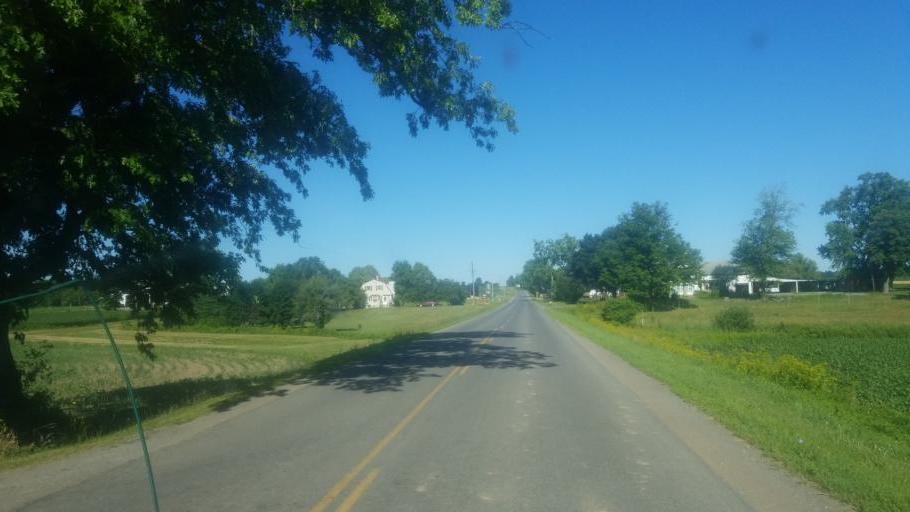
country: US
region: New York
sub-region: Ontario County
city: Clifton Springs
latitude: 42.8369
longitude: -77.1548
